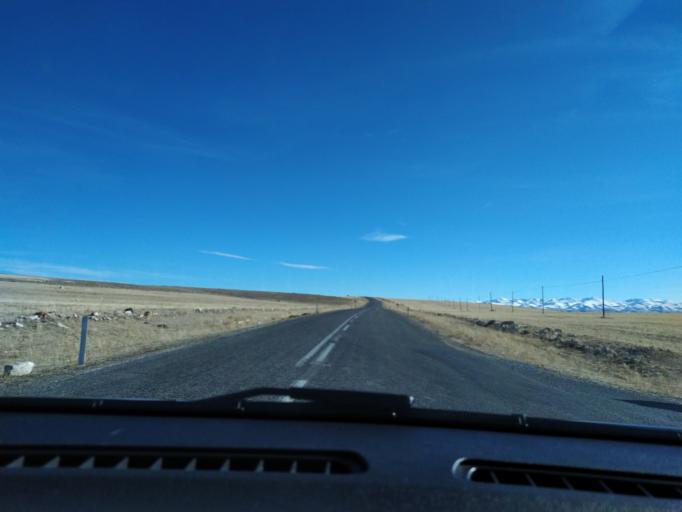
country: TR
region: Kayseri
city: Orensehir
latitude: 38.9519
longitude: 36.6906
